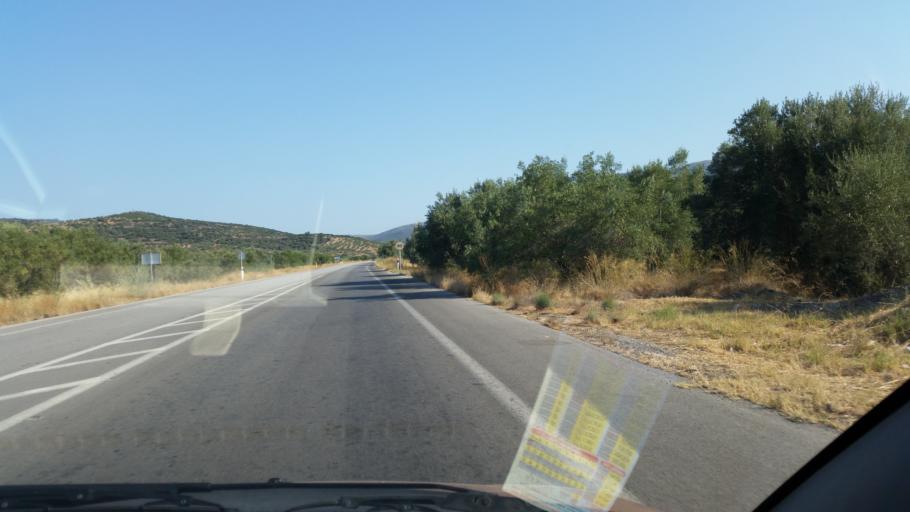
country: GR
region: Peloponnese
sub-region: Nomos Argolidos
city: Koutsopodi
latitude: 37.7208
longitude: 22.7352
